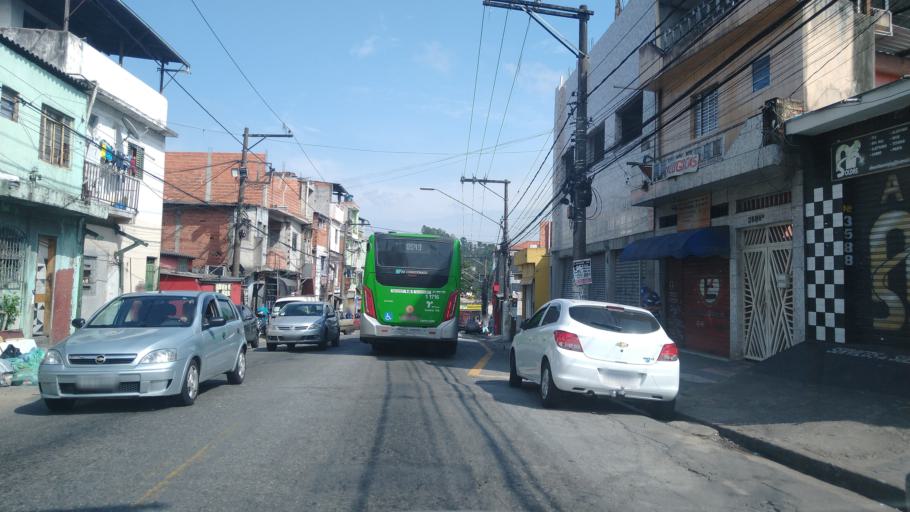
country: BR
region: Sao Paulo
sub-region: Caieiras
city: Caieiras
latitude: -23.4547
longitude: -46.6960
